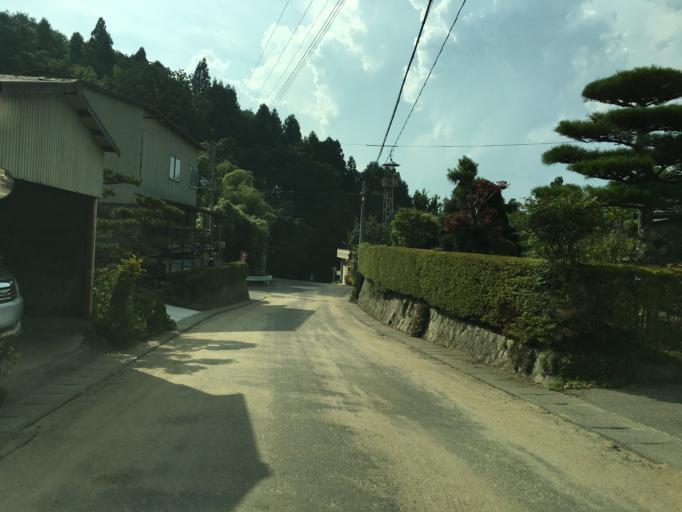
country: JP
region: Fukushima
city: Miharu
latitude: 37.4181
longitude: 140.4435
